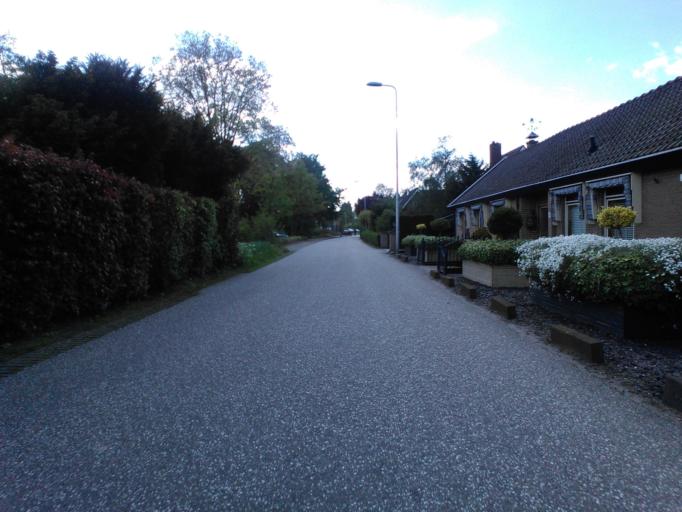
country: NL
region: South Holland
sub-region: Gemeente Ridderkerk
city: Ridderkerk
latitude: 51.8495
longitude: 4.6124
